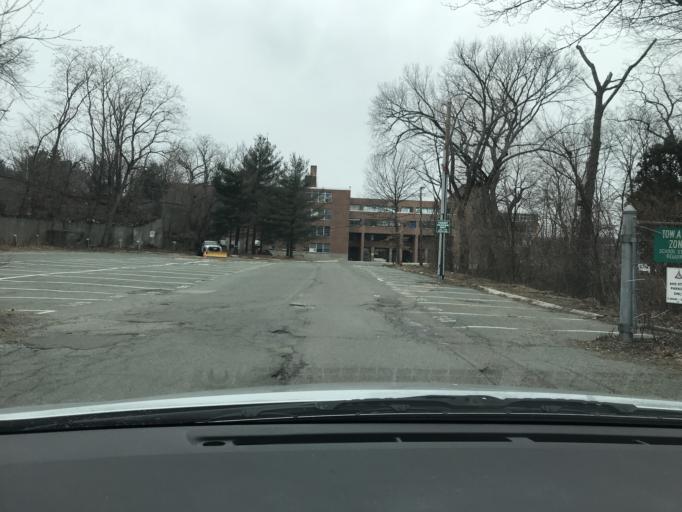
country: US
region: Massachusetts
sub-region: Middlesex County
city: Arlington
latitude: 42.4178
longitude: -71.1593
